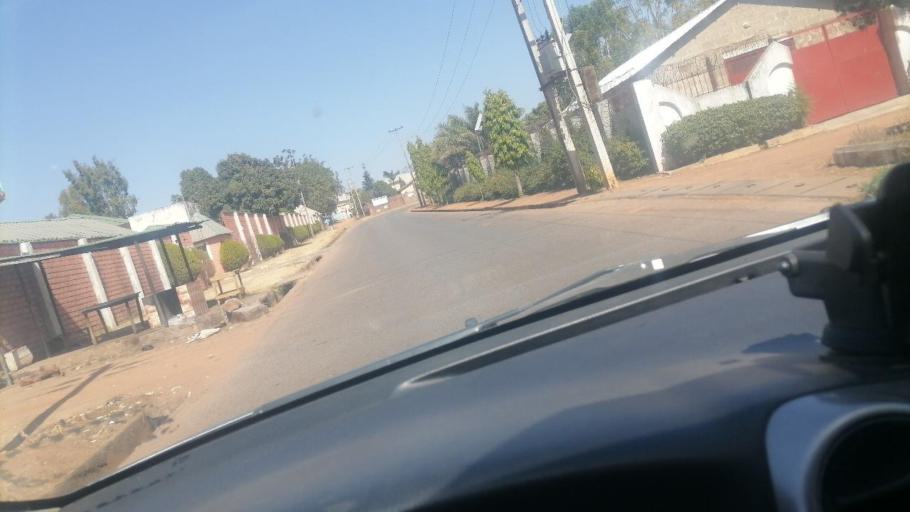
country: NG
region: Plateau
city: Jos
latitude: 9.8663
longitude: 8.9065
